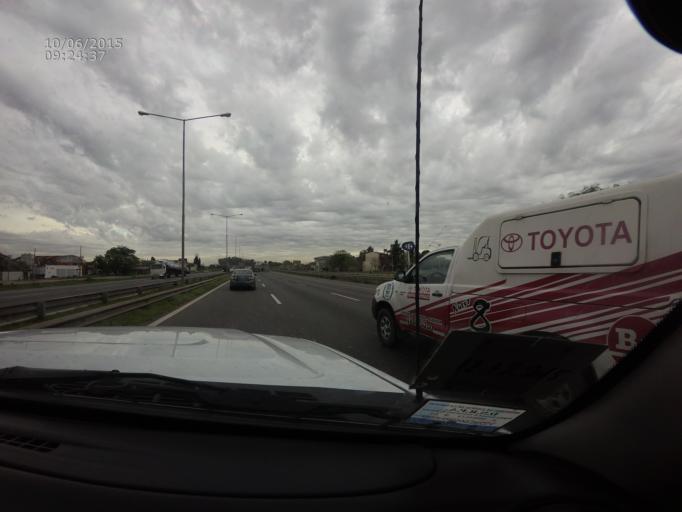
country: AR
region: Buenos Aires
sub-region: Partido de Campana
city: Campana
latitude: -34.1871
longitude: -58.9467
